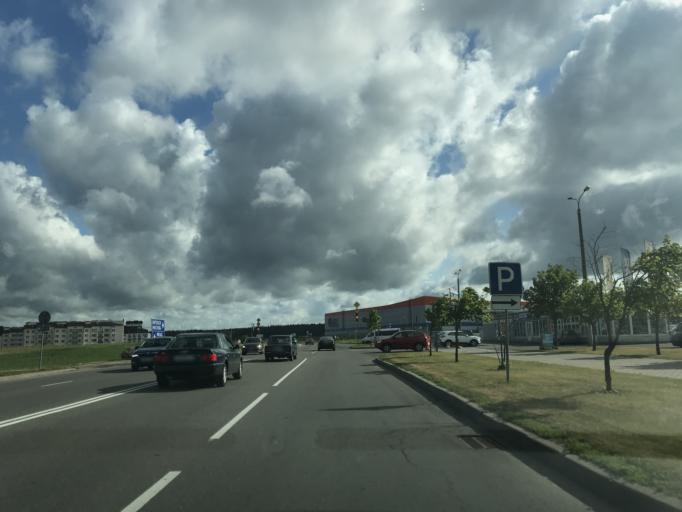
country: BY
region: Minsk
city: Borovlyany
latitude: 53.9657
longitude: 27.6220
